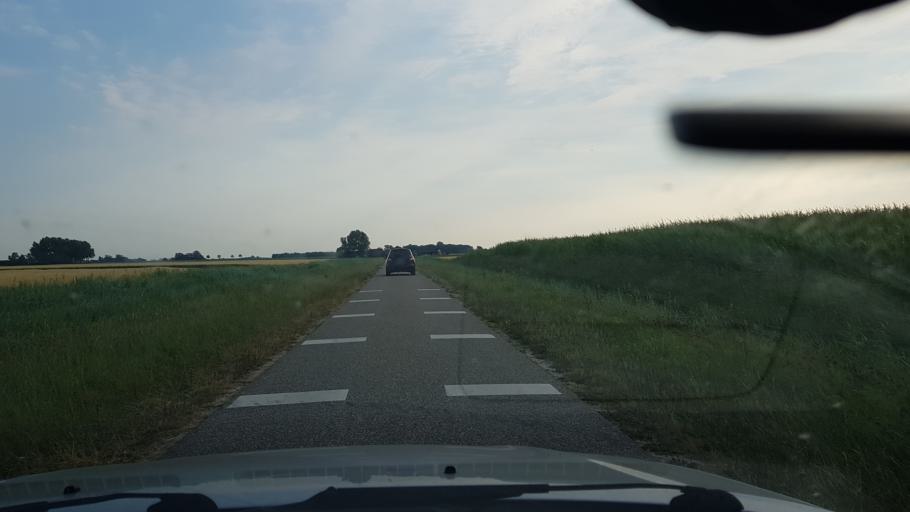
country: NL
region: Friesland
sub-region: Gemeente Dongeradeel
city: Holwerd
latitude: 53.3450
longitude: 5.8730
